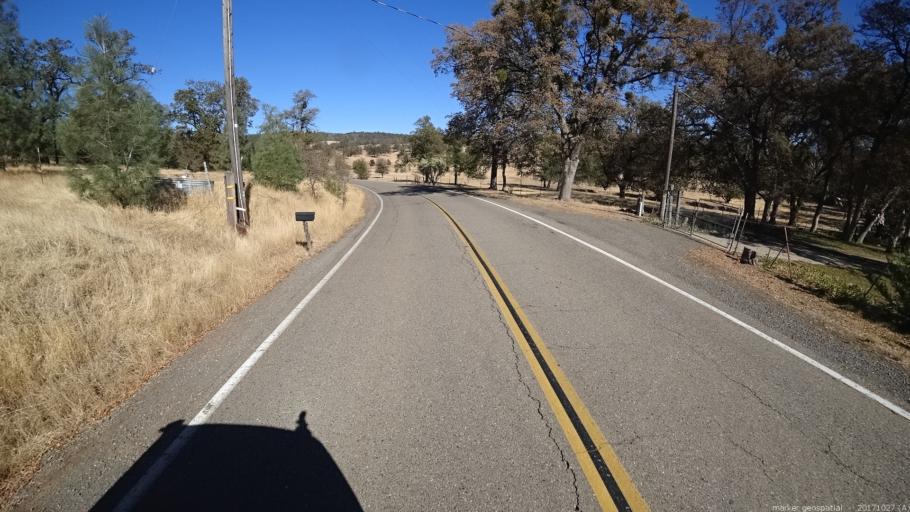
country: US
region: California
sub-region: Shasta County
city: Bella Vista
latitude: 40.6987
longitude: -122.0386
